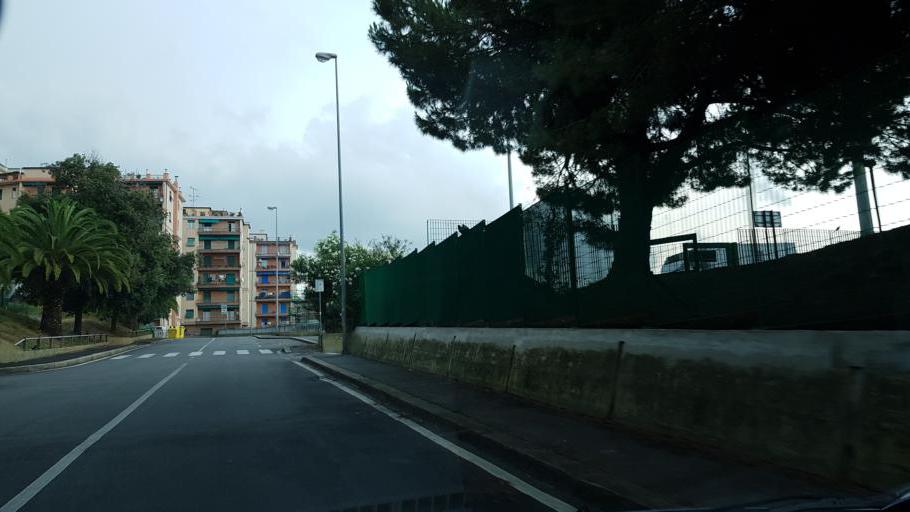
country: IT
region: Liguria
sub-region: Provincia di Genova
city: San Teodoro
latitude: 44.4286
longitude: 8.8337
